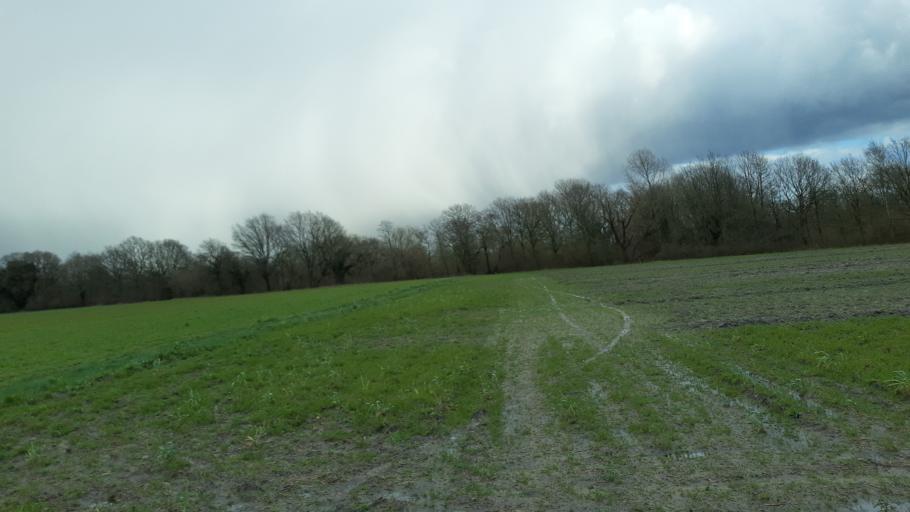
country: NL
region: Drenthe
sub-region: Gemeente Borger-Odoorn
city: Borger
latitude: 52.8470
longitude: 6.6568
